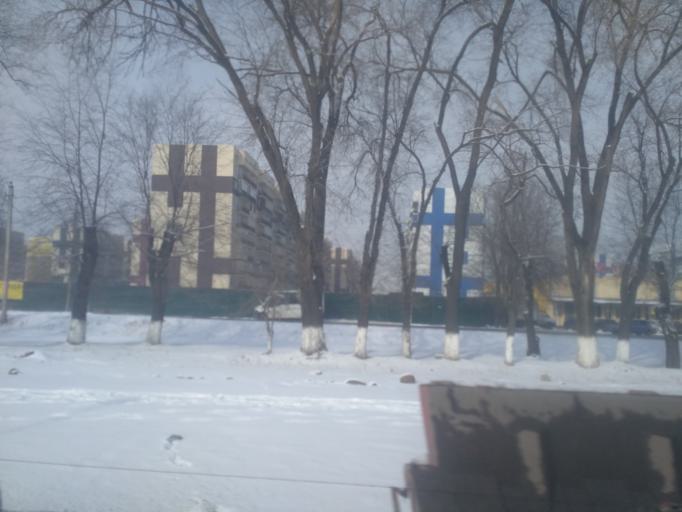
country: KZ
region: Almaty Oblysy
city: Burunday
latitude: 43.2279
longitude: 76.7520
